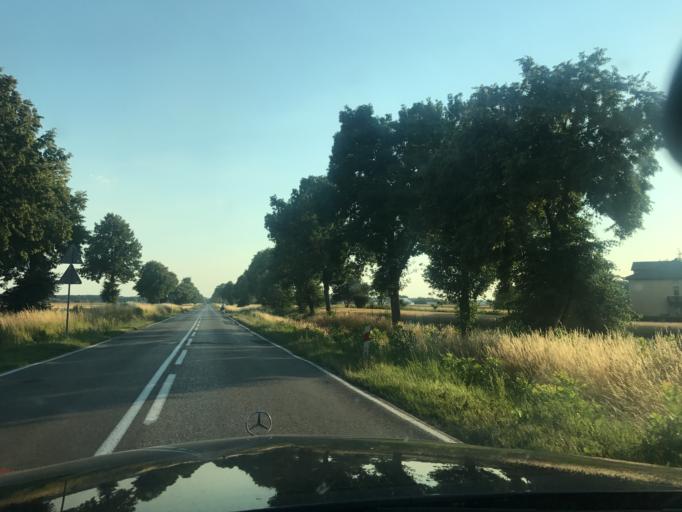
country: PL
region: Lublin Voivodeship
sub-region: Powiat parczewski
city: Jablon
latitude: 51.7162
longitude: 23.0888
